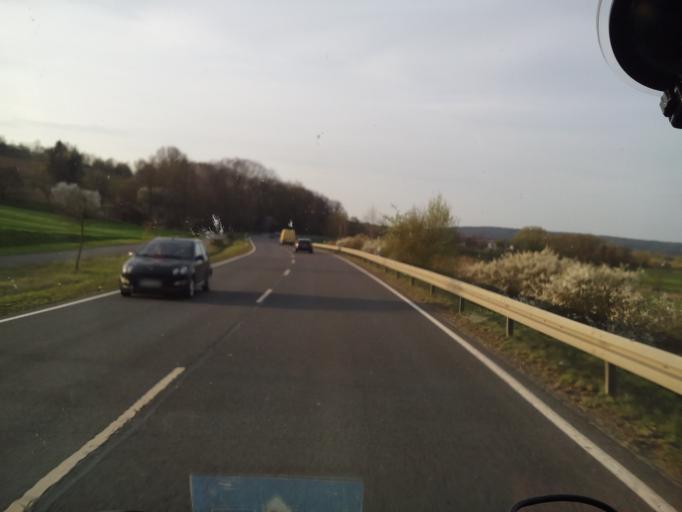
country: DE
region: Bavaria
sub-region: Upper Franconia
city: Reckendorf
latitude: 50.0102
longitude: 10.8277
